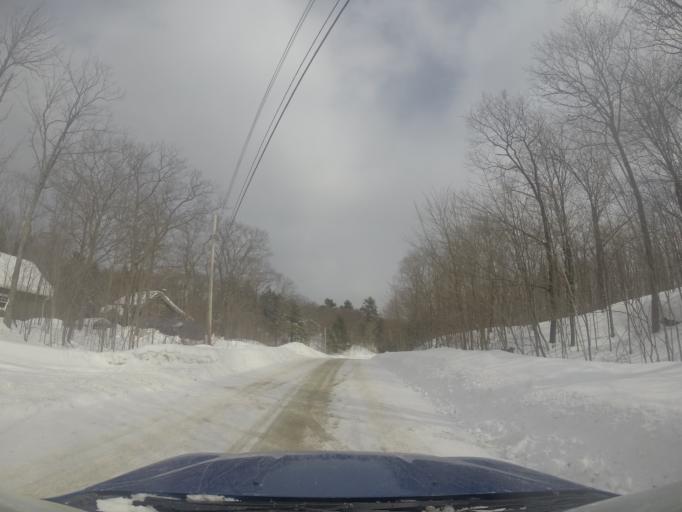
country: CA
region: Ontario
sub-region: Parry Sound District
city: Parry Sound
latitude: 45.3896
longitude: -80.0323
